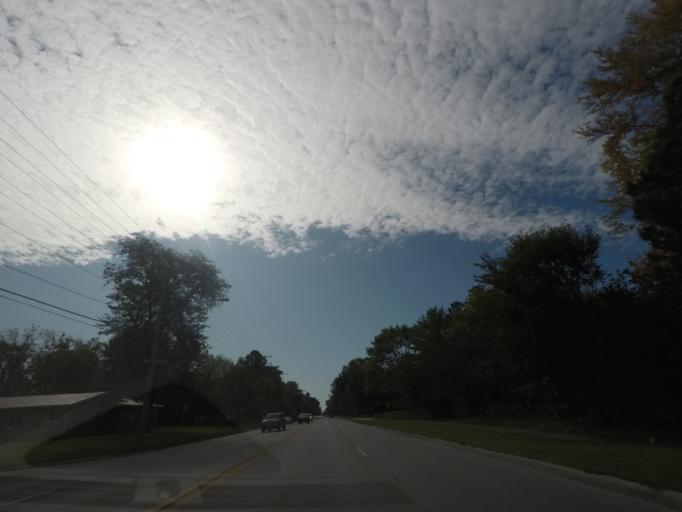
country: US
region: Iowa
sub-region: Story County
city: Ames
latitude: 42.0404
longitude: -93.6207
